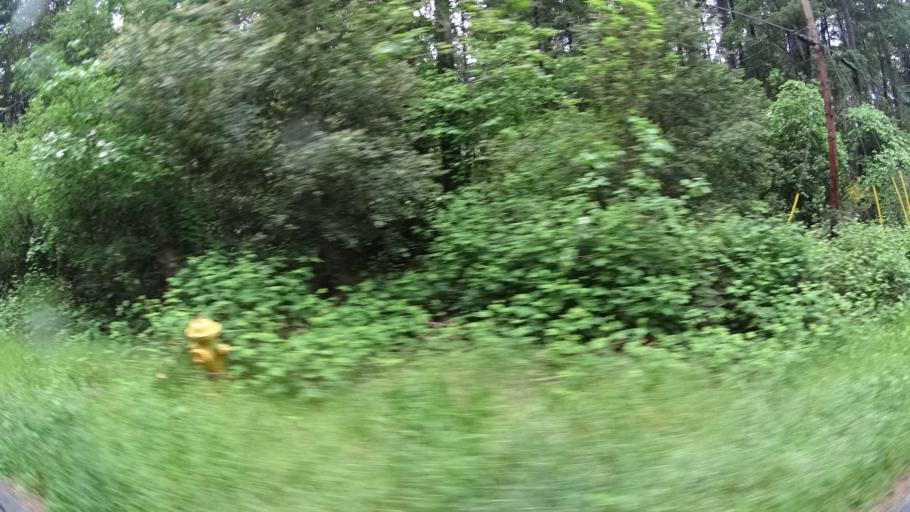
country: US
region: California
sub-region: Humboldt County
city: Willow Creek
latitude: 41.0492
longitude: -123.6653
